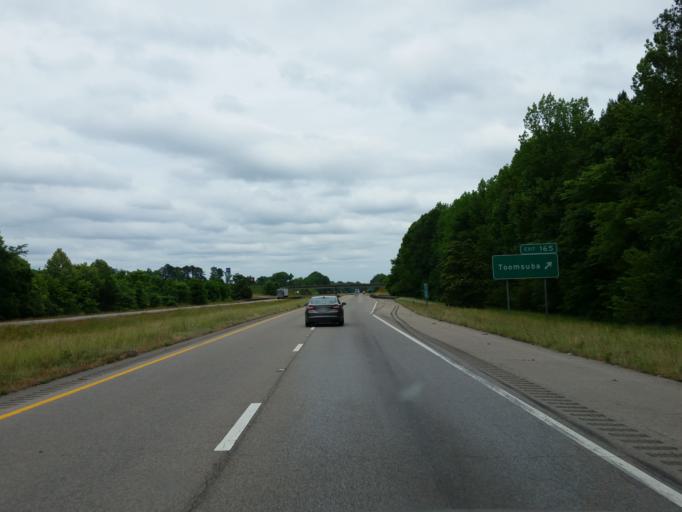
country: US
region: Mississippi
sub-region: Lauderdale County
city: Marion
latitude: 32.4134
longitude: -88.5117
